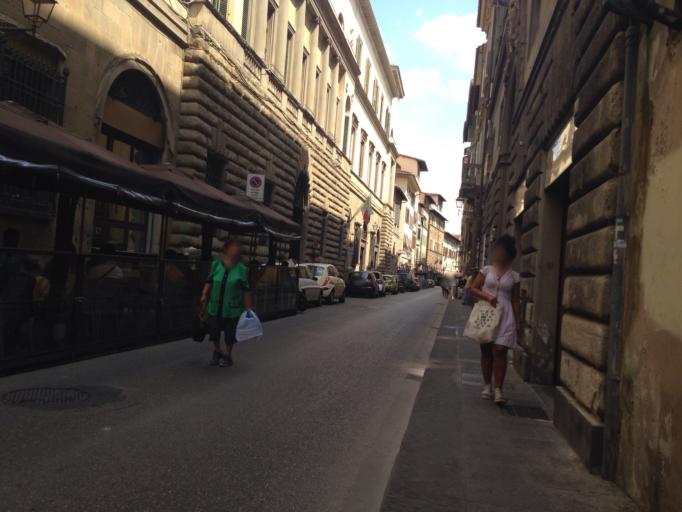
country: IT
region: Tuscany
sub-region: Province of Florence
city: Florence
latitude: 43.7708
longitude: 11.2589
